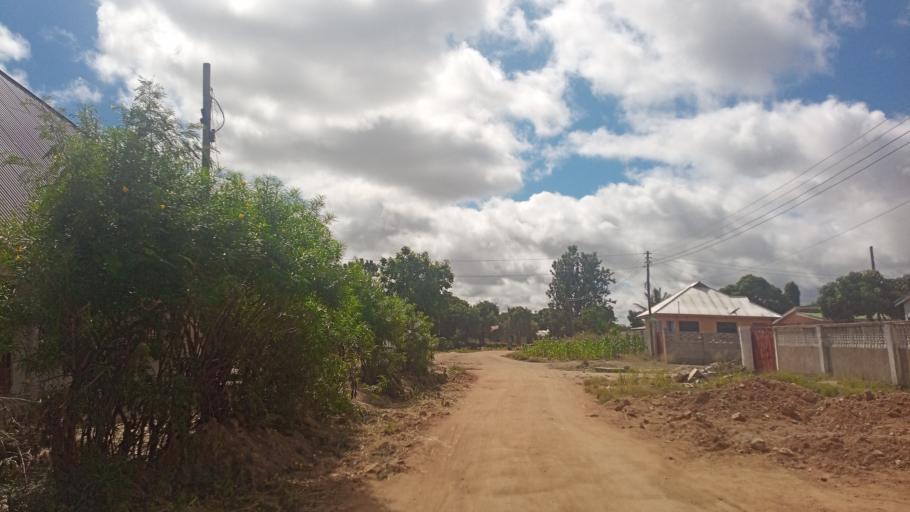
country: TZ
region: Dodoma
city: Dodoma
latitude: -6.1907
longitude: 35.7332
